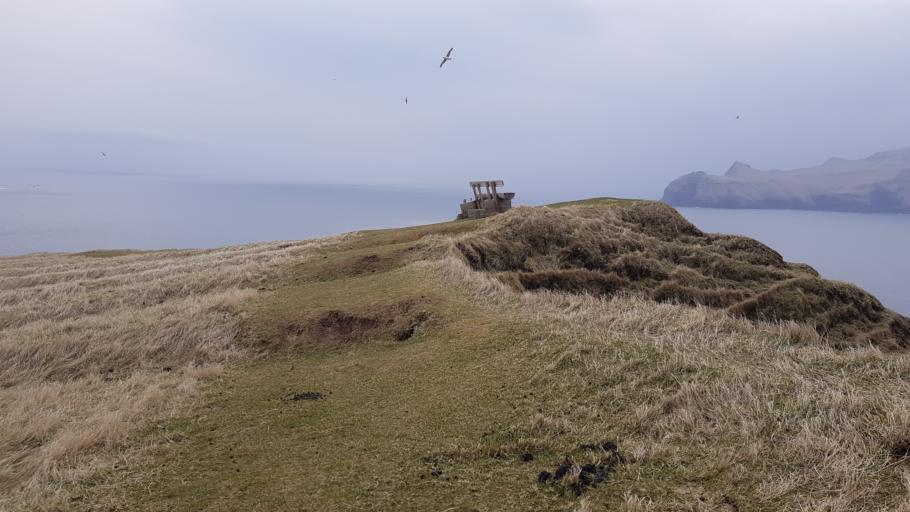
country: FO
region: Vagar
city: Sorvagur
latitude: 62.1108
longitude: -7.4431
